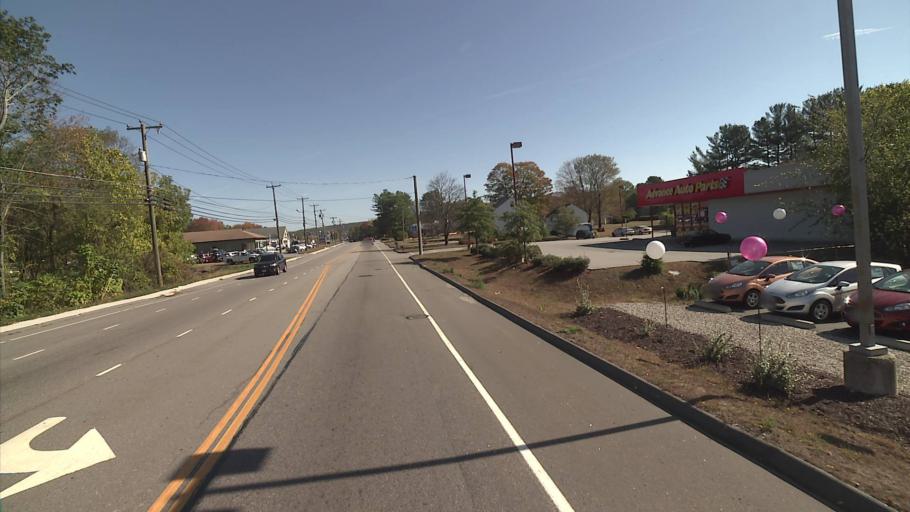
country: US
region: Connecticut
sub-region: Windham County
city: East Brooklyn
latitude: 41.7972
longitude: -71.9109
